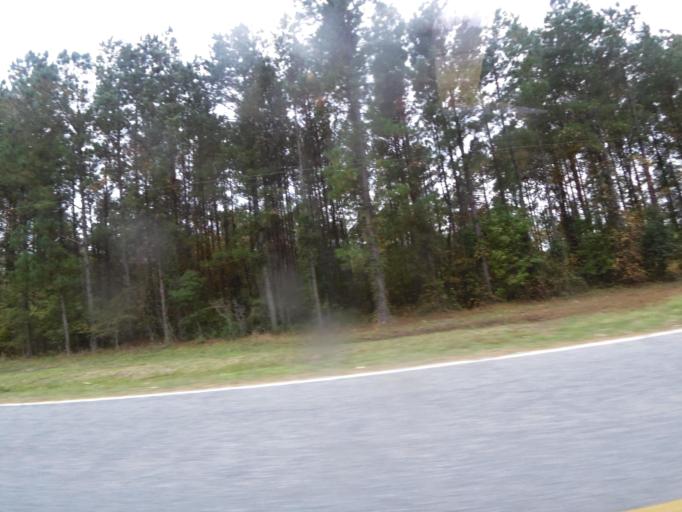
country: US
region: Georgia
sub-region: Charlton County
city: Folkston
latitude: 30.9167
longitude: -82.0857
